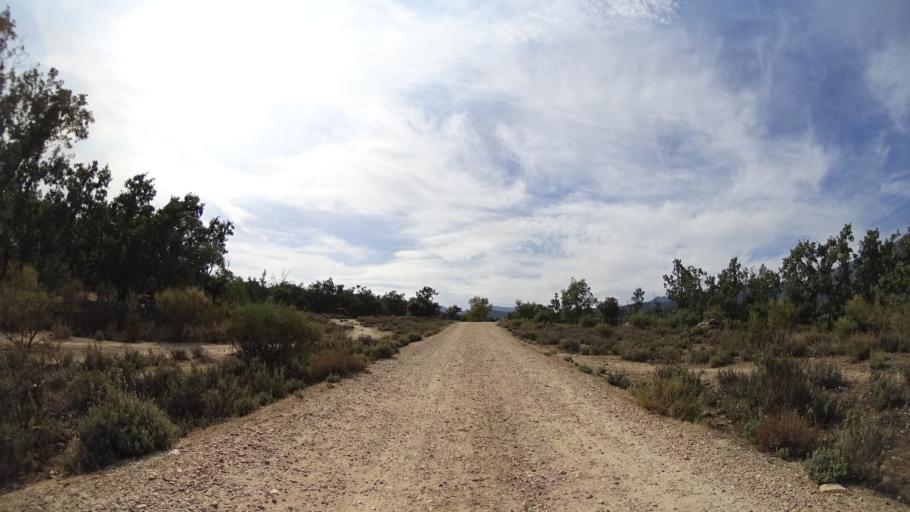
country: ES
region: Madrid
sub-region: Provincia de Madrid
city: Becerril de la Sierra
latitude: 40.6996
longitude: -3.9782
